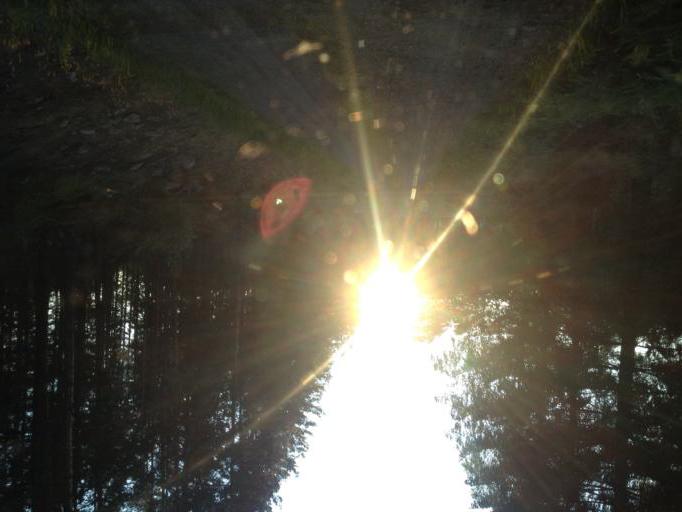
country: SE
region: Kalmar
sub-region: Vasterviks Kommun
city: Overum
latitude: 58.0012
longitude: 16.1247
